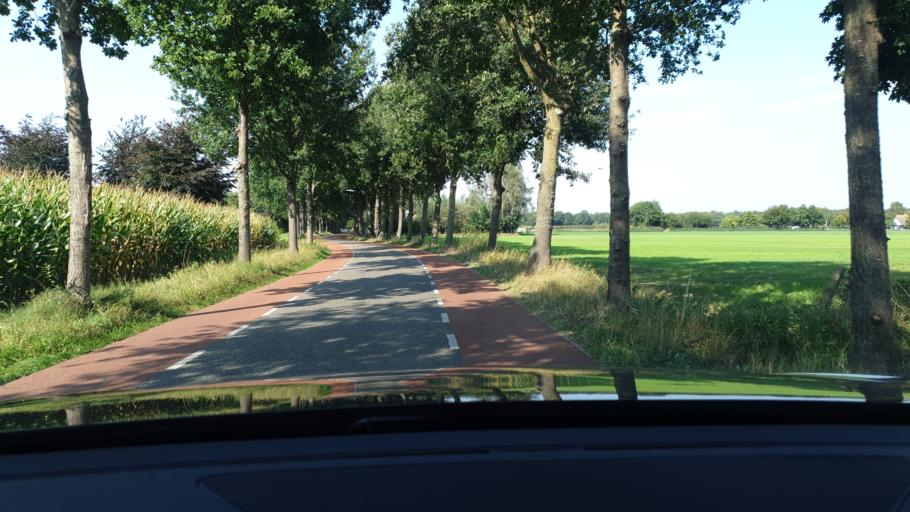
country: NL
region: North Brabant
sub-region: Gemeente Bernheze
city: Loosbroek
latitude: 51.6584
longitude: 5.4640
